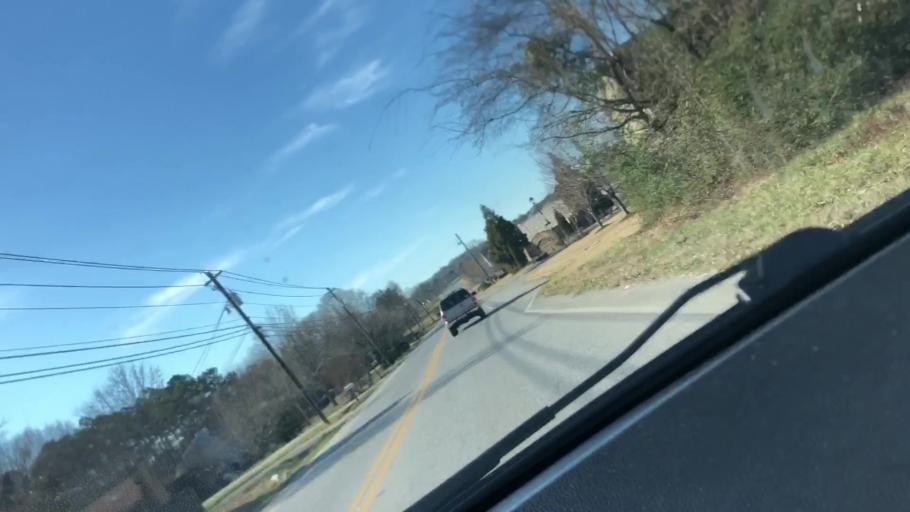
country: US
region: Georgia
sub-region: Bartow County
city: Cartersville
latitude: 34.2226
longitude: -84.8088
